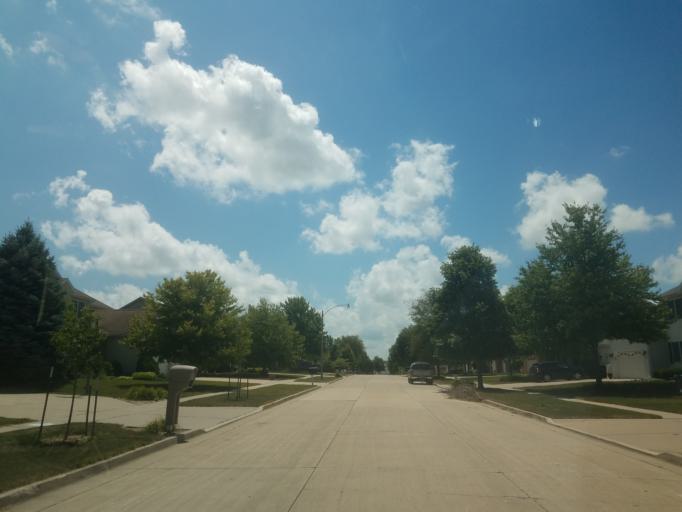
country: US
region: Illinois
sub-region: McLean County
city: Normal
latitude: 40.4978
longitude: -88.9139
